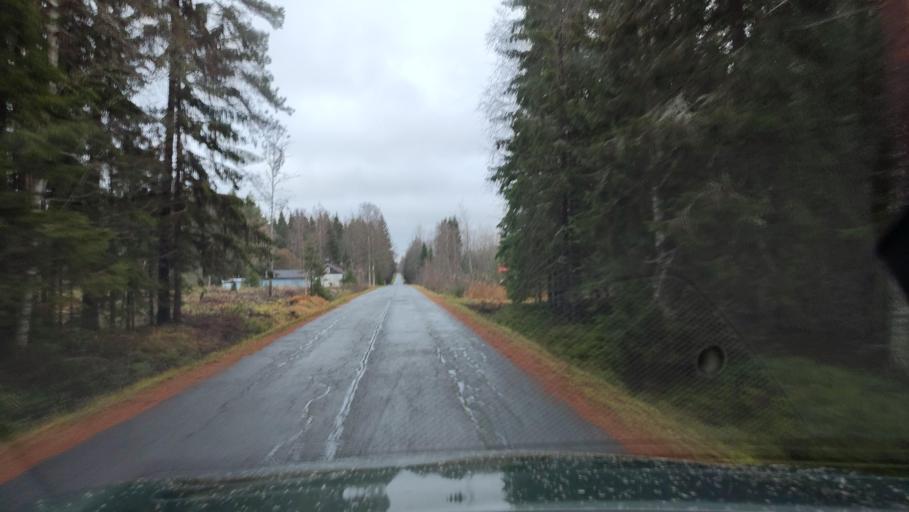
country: FI
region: Southern Ostrobothnia
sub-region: Suupohja
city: Teuva
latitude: 62.4576
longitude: 21.5860
